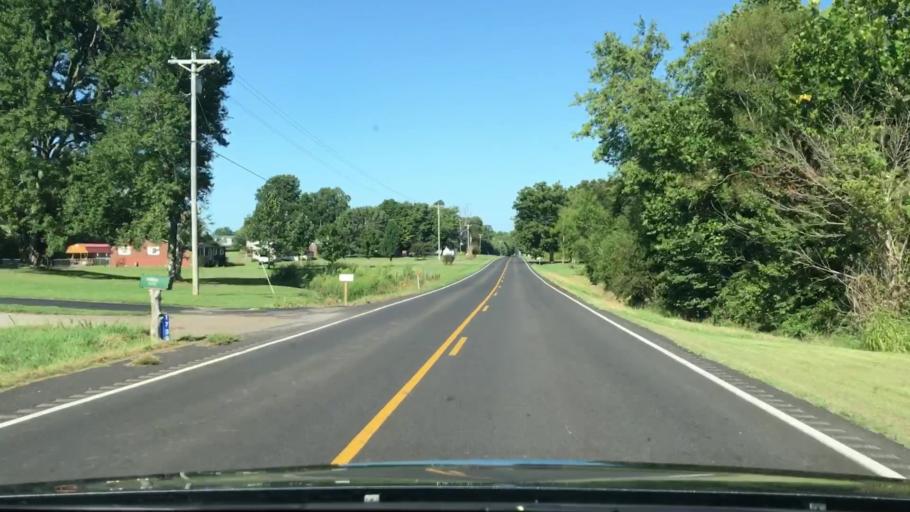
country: US
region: Kentucky
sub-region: Marshall County
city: Benton
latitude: 36.7647
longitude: -88.3351
